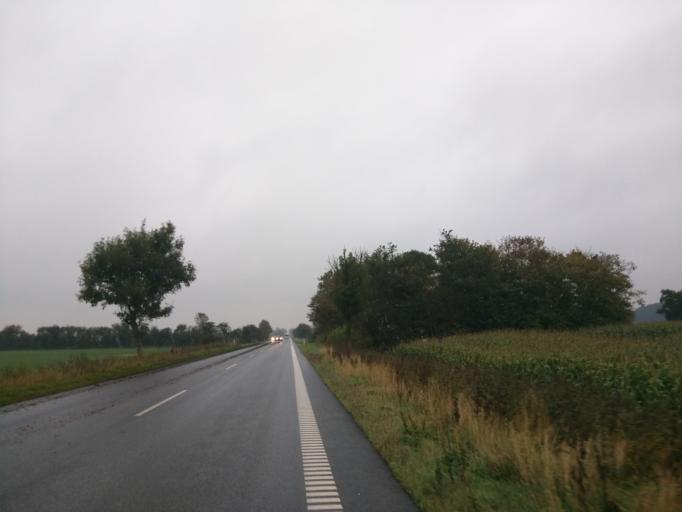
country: DK
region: Central Jutland
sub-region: Silkeborg Kommune
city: Kjellerup
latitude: 56.3704
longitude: 9.4397
